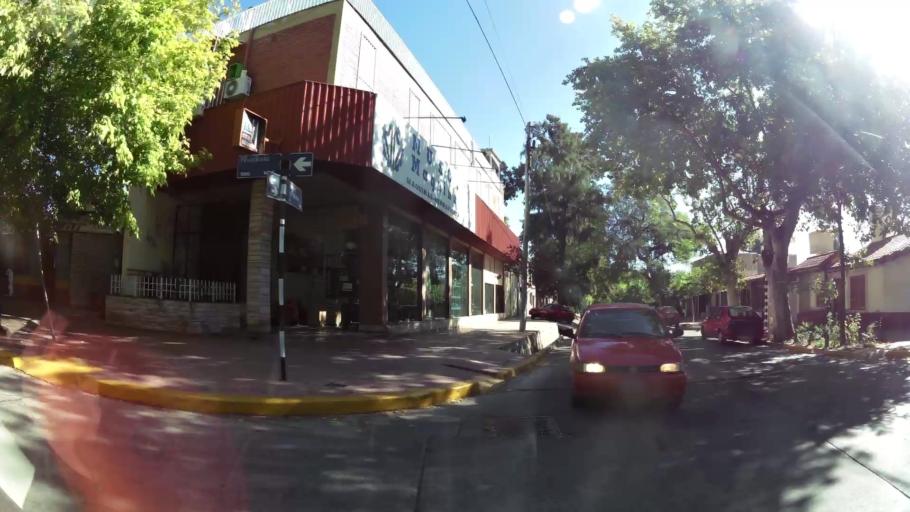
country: AR
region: Mendoza
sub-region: Departamento de Godoy Cruz
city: Godoy Cruz
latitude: -32.9238
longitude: -68.8558
